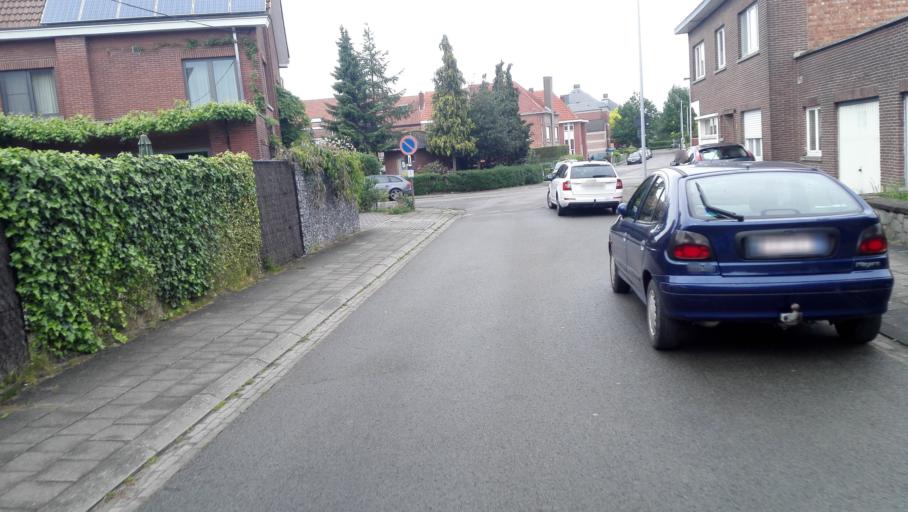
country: BE
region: Flanders
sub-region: Provincie Vlaams-Brabant
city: Leuven
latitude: 50.8795
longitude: 4.7239
